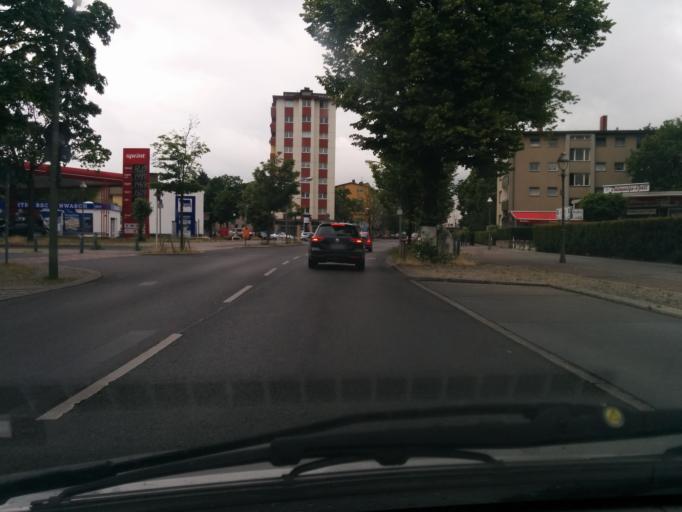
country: DE
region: Berlin
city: Spandau
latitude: 52.5362
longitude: 13.1921
